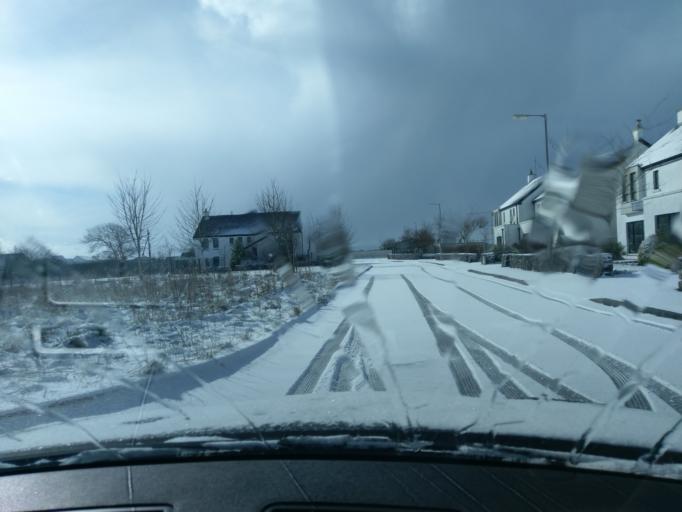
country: IE
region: Connaught
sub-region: County Galway
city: Oranmore
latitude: 53.1834
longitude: -8.9044
